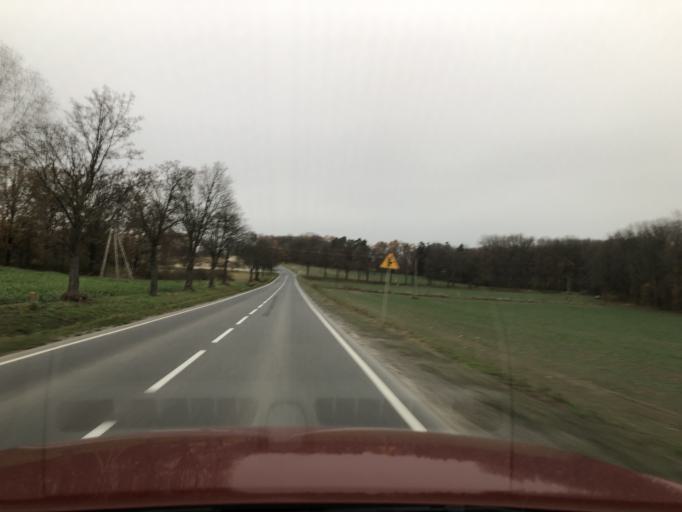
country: PL
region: Lower Silesian Voivodeship
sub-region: Powiat swidnicki
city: Zarow
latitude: 50.9692
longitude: 16.4972
